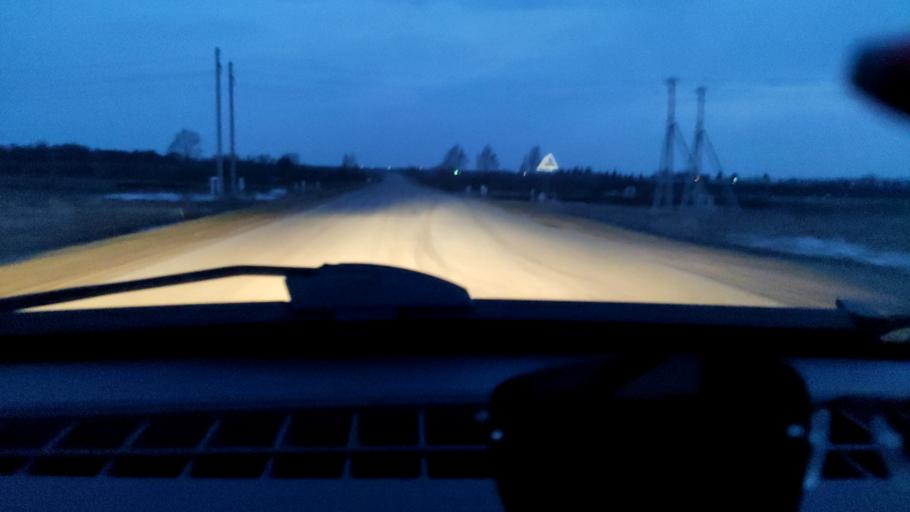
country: RU
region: Bashkortostan
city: Kabakovo
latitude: 54.4880
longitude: 56.1886
